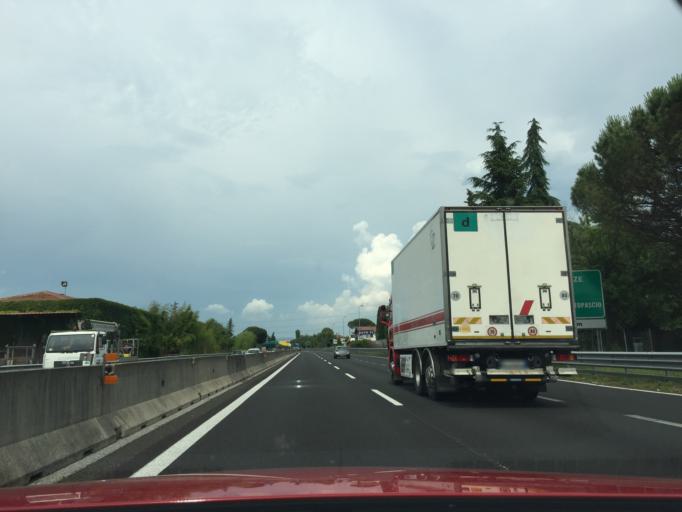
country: IT
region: Tuscany
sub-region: Provincia di Lucca
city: Altopascio
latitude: 43.8186
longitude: 10.6798
